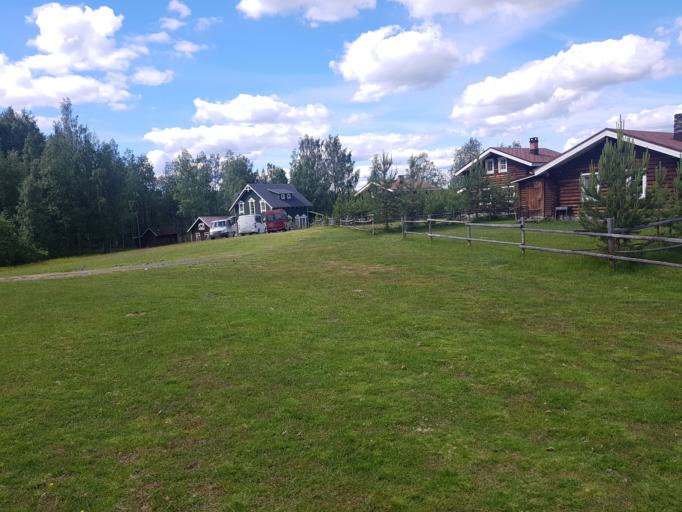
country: RU
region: Republic of Karelia
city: Kostomuksha
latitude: 64.8947
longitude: 30.4775
